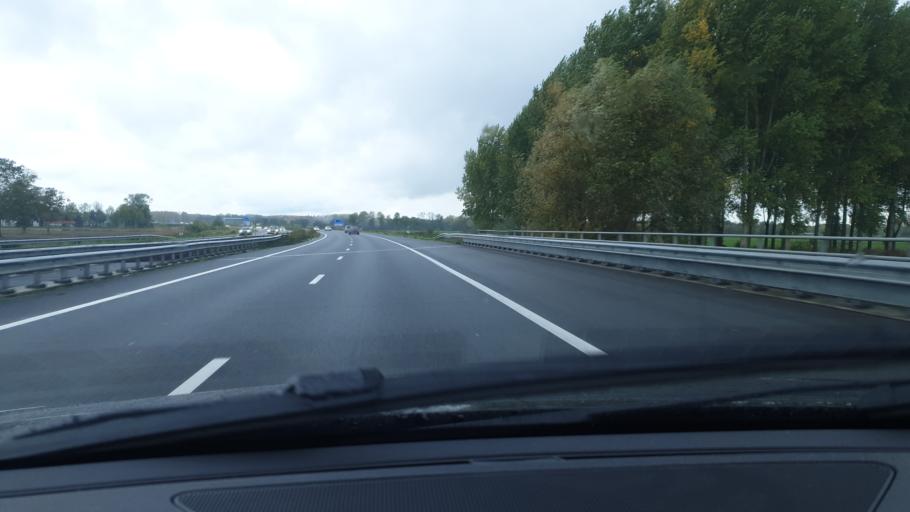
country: NL
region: North Brabant
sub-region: Gemeente Veghel
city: Eerde
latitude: 51.6320
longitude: 5.5166
